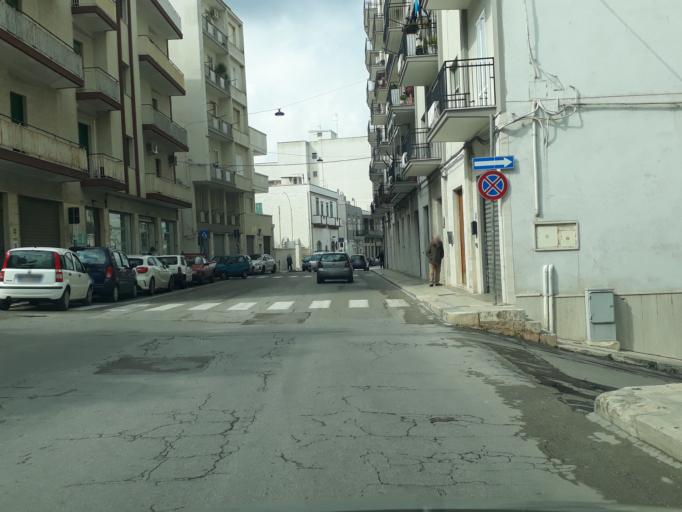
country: IT
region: Apulia
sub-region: Provincia di Bari
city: Locorotondo
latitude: 40.7549
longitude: 17.3290
